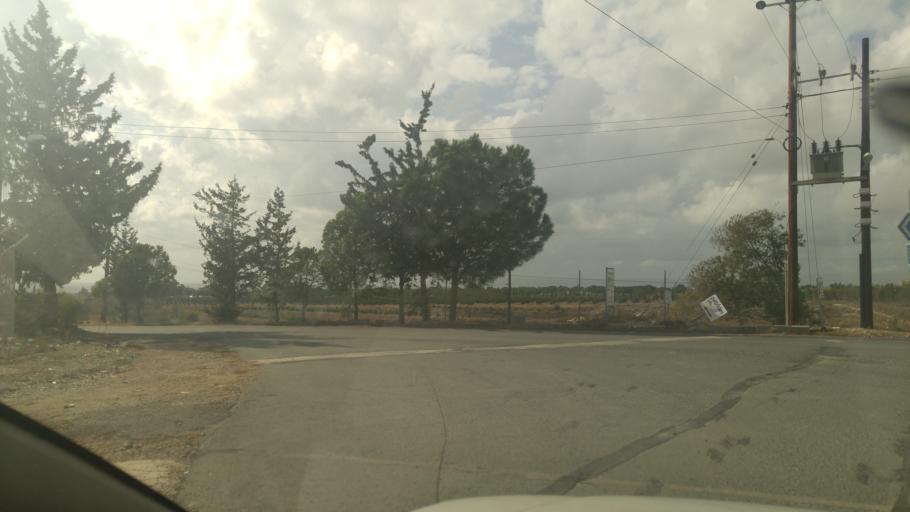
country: CY
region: Pafos
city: Paphos
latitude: 34.7507
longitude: 32.4881
